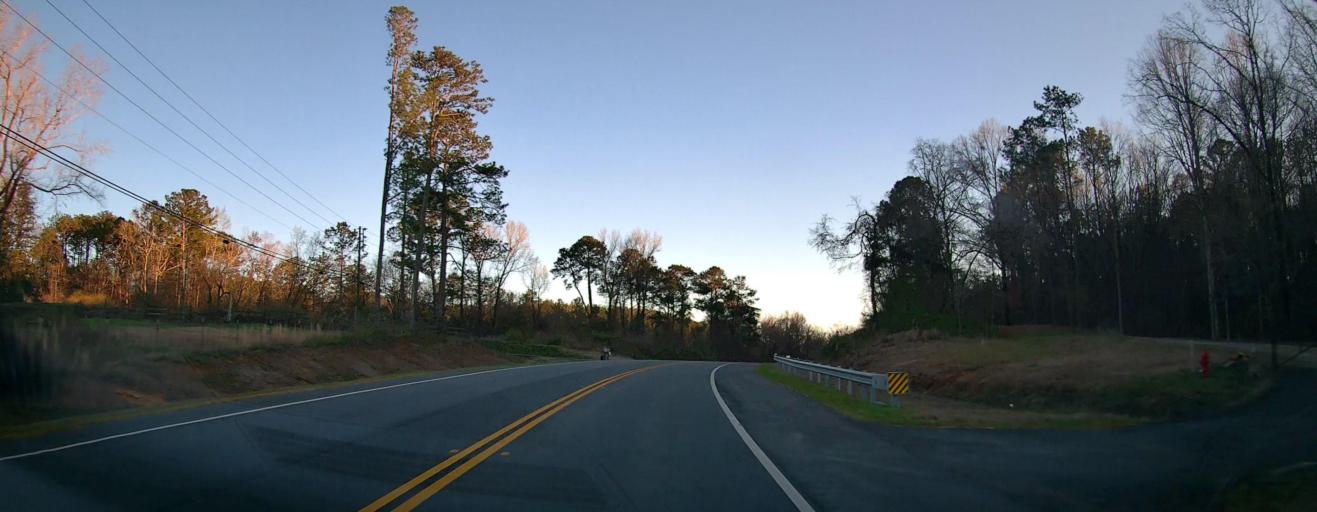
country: US
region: Alabama
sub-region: Lee County
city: Smiths Station
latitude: 32.6168
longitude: -85.0270
